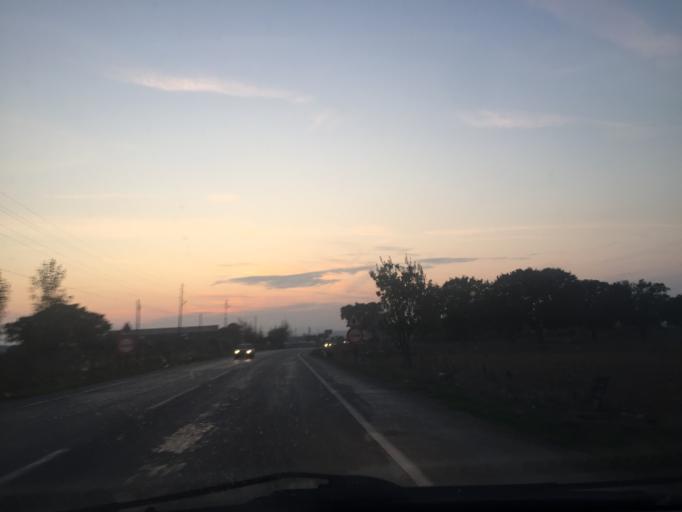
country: TR
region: Canakkale
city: Bayramic
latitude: 39.7775
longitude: 26.4910
